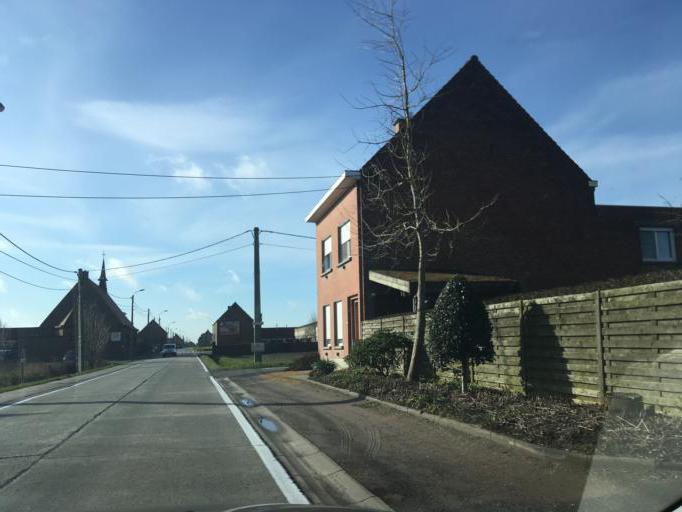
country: BE
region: Flanders
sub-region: Provincie West-Vlaanderen
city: Roeselare
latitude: 50.9064
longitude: 3.1432
